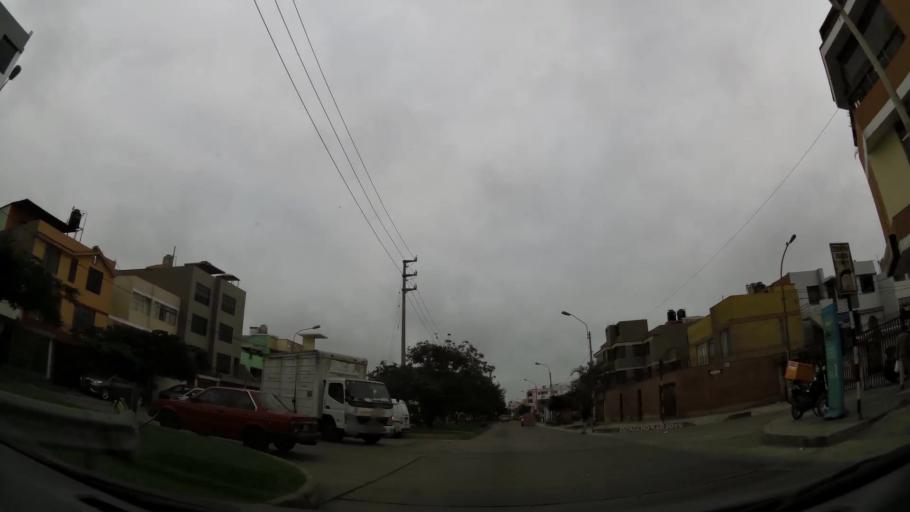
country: PE
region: Lima
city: Lima
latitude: -12.0645
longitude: -77.0671
